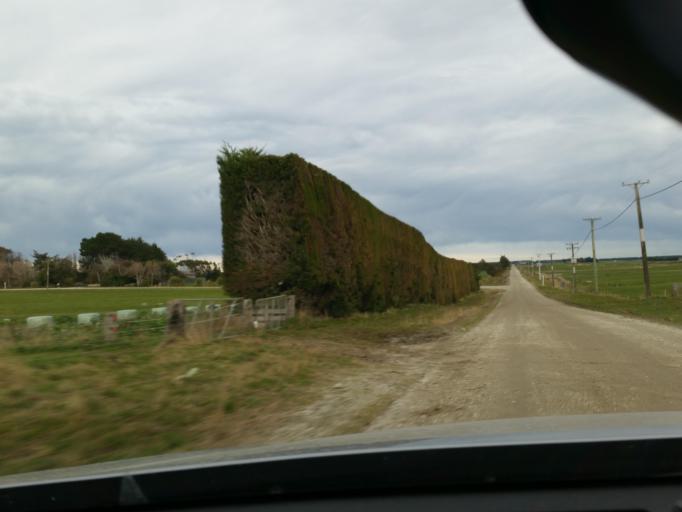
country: NZ
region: Southland
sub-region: Invercargill City
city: Invercargill
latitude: -46.4217
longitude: 168.5061
